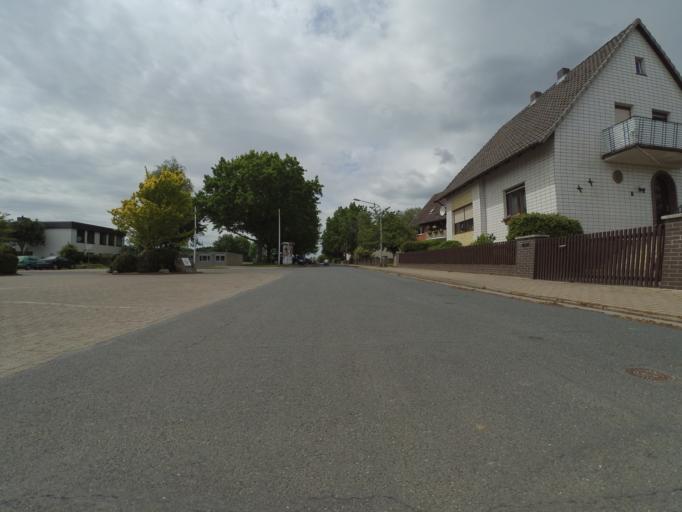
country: DE
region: Lower Saxony
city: Wunstorf
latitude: 52.4460
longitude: 9.4197
